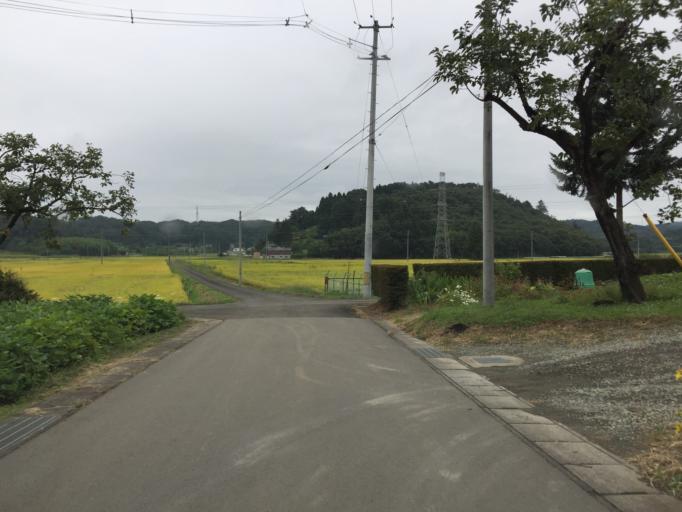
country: JP
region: Fukushima
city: Nihommatsu
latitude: 37.6517
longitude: 140.4451
